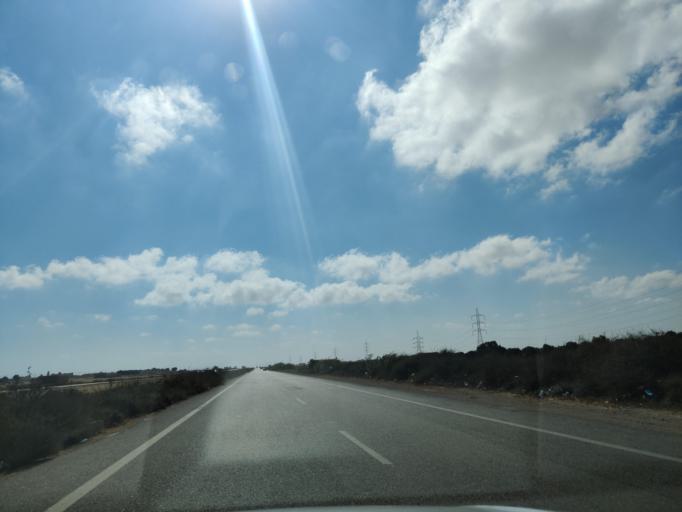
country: EG
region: Muhafazat Matruh
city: Al `Alamayn
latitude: 31.0541
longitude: 28.2664
